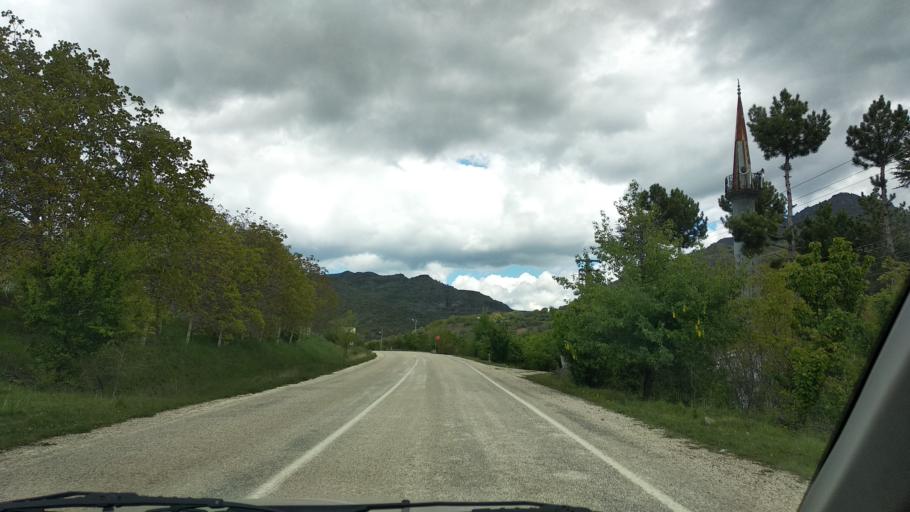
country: TR
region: Bolu
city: Seben
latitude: 40.4191
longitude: 31.5831
